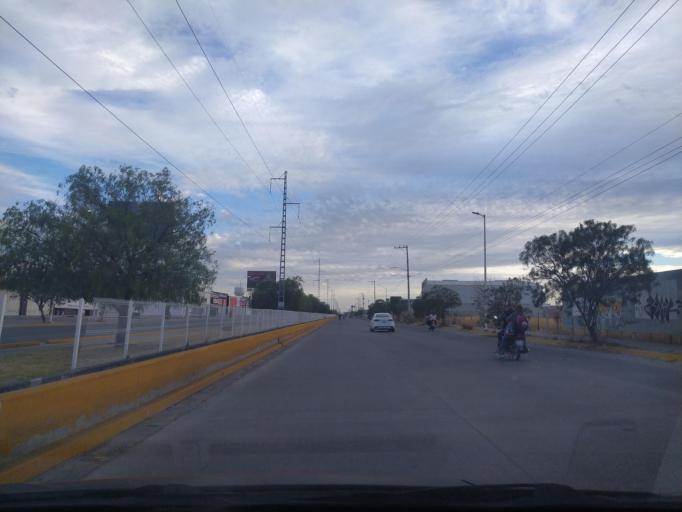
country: LA
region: Oudomxai
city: Muang La
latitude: 21.0233
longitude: 101.8696
